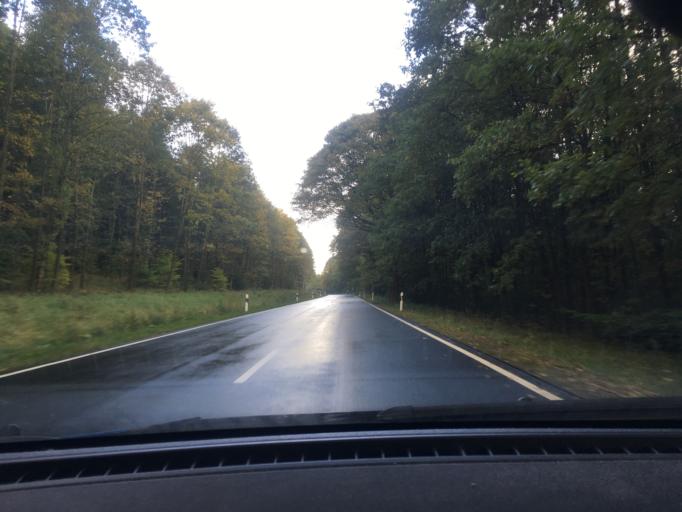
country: DE
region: Lower Saxony
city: Bevern
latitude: 51.7632
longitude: 9.5279
